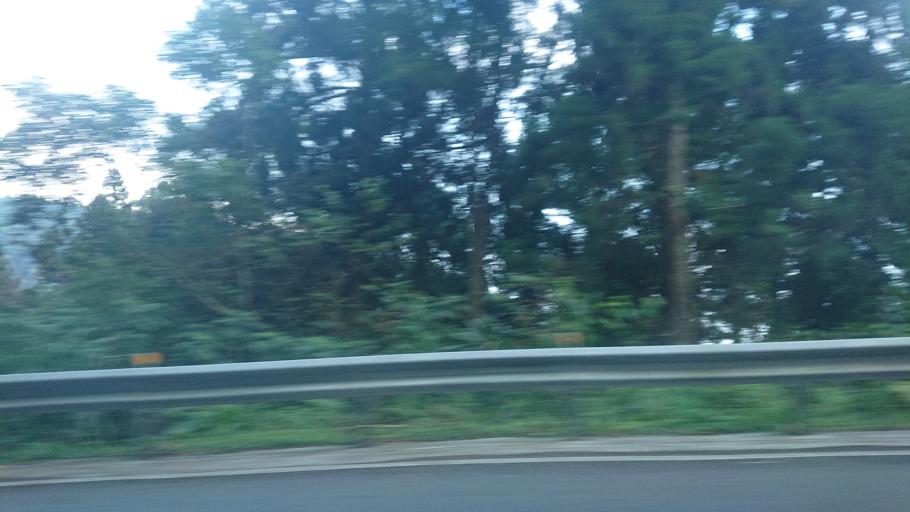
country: TW
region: Taiwan
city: Lugu
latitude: 23.4873
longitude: 120.7465
